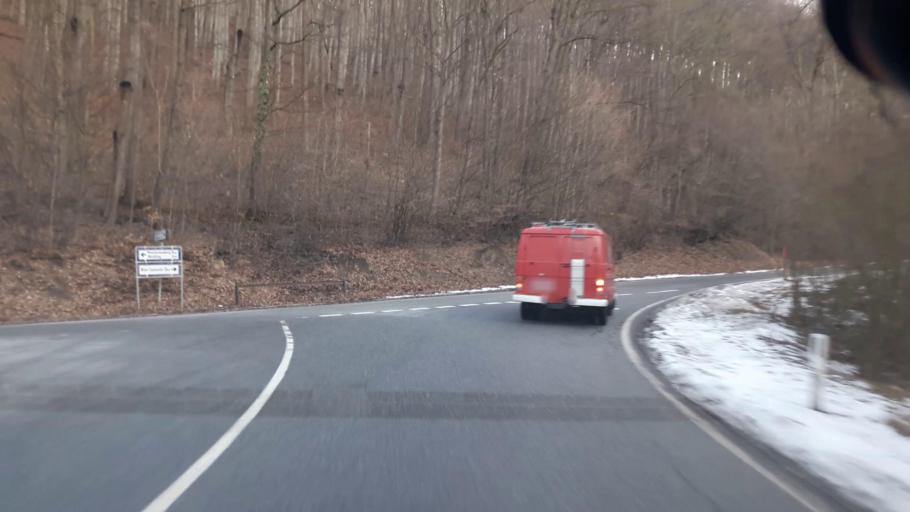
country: AT
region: Lower Austria
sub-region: Politischer Bezirk Wien-Umgebung
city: Klosterneuburg
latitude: 48.2669
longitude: 16.2727
